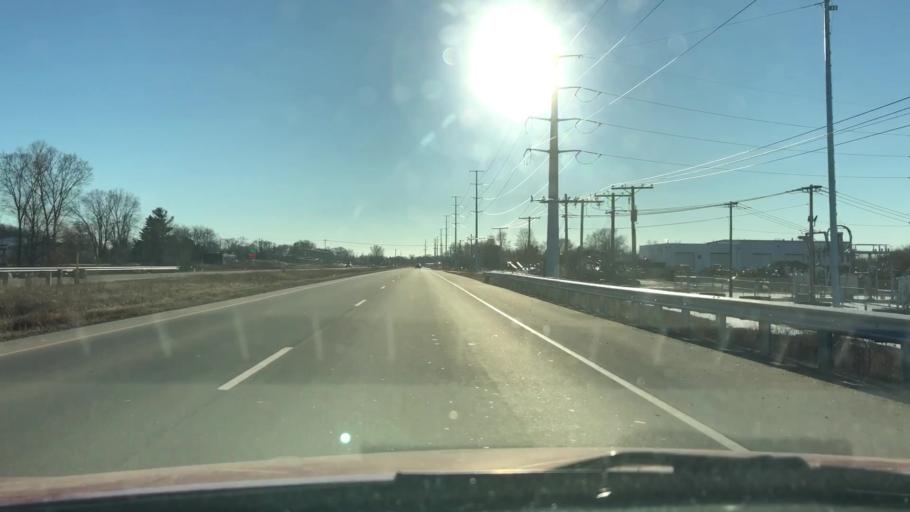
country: US
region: Wisconsin
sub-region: Brown County
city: Ashwaubenon
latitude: 44.4653
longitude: -88.0700
